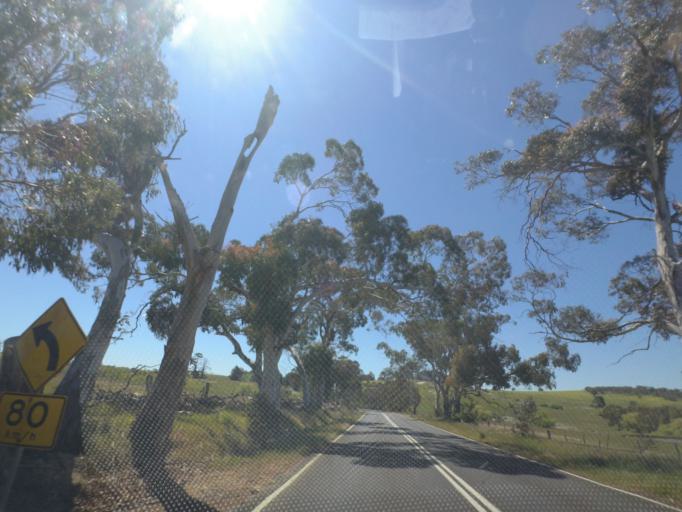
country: AU
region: Victoria
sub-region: Hume
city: Sunbury
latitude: -37.1495
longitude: 144.7712
